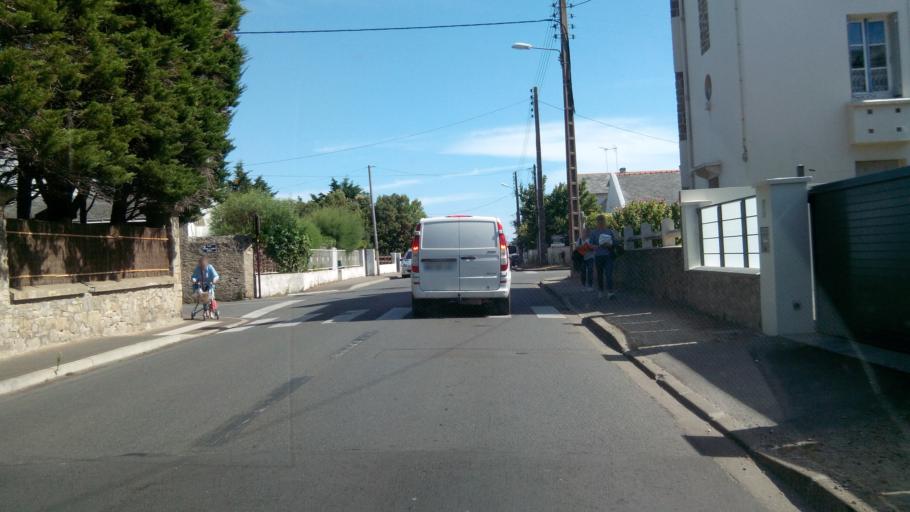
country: FR
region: Pays de la Loire
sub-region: Departement de la Loire-Atlantique
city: Le Croisic
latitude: 47.2873
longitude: -2.5089
